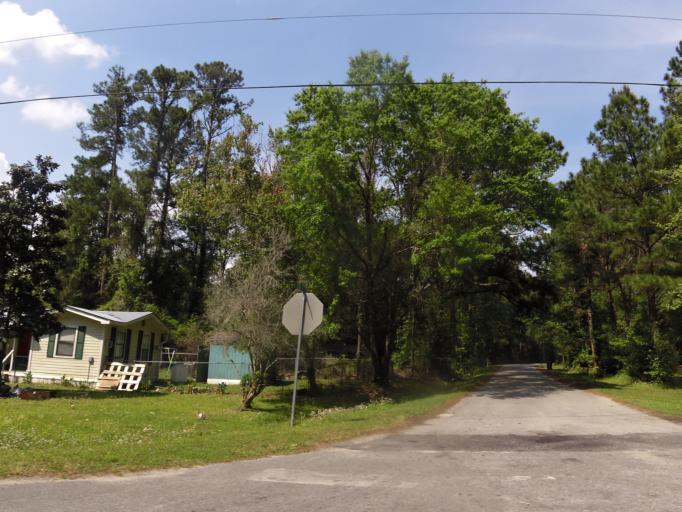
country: US
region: Georgia
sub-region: Camden County
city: Kingsland
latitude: 30.8042
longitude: -81.7420
